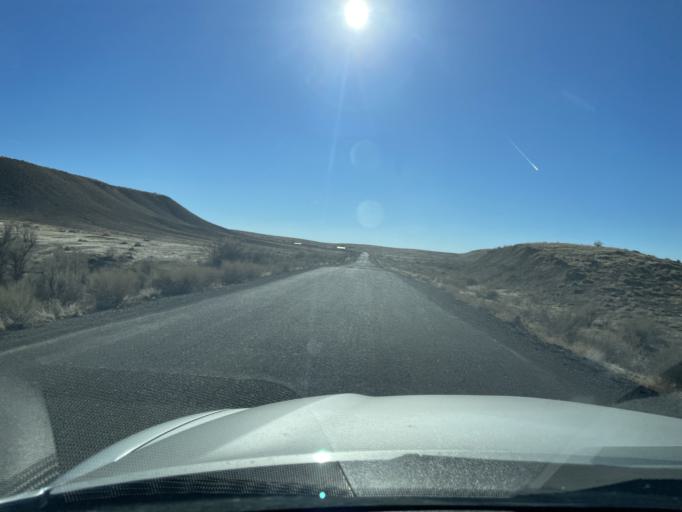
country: US
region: Colorado
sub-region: Mesa County
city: Loma
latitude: 39.2051
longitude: -109.1118
